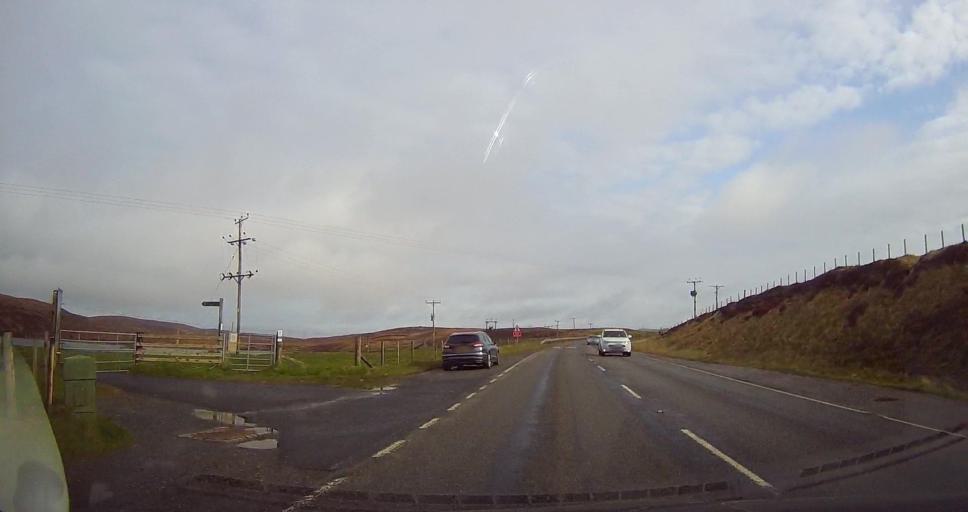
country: GB
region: Scotland
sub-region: Shetland Islands
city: Lerwick
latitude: 60.1119
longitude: -1.2191
